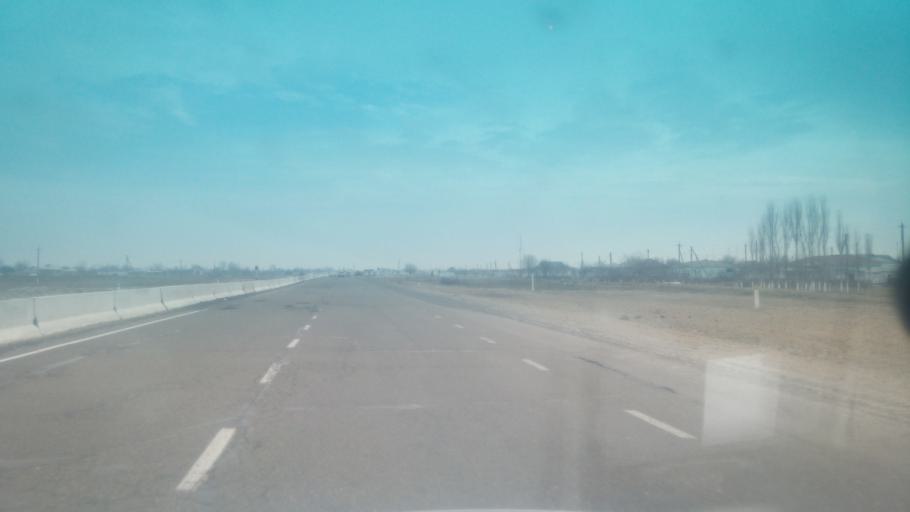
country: KZ
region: Ongtustik Qazaqstan
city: Myrzakent
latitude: 40.5075
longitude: 68.5084
